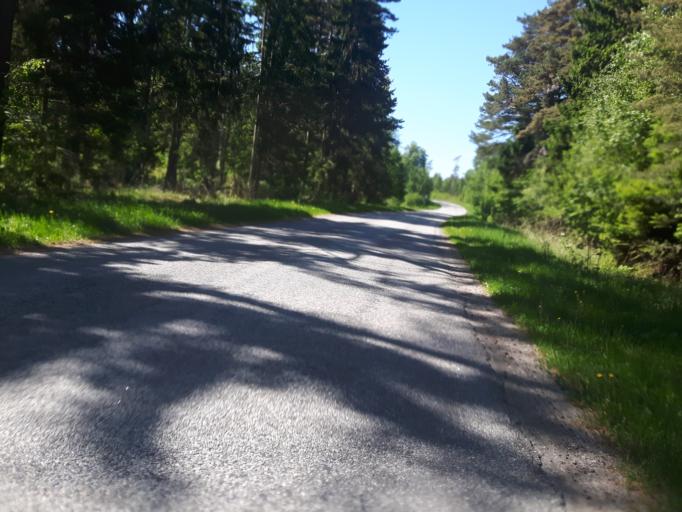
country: EE
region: Laeaene-Virumaa
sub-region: Haljala vald
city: Haljala
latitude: 59.5507
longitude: 26.3720
